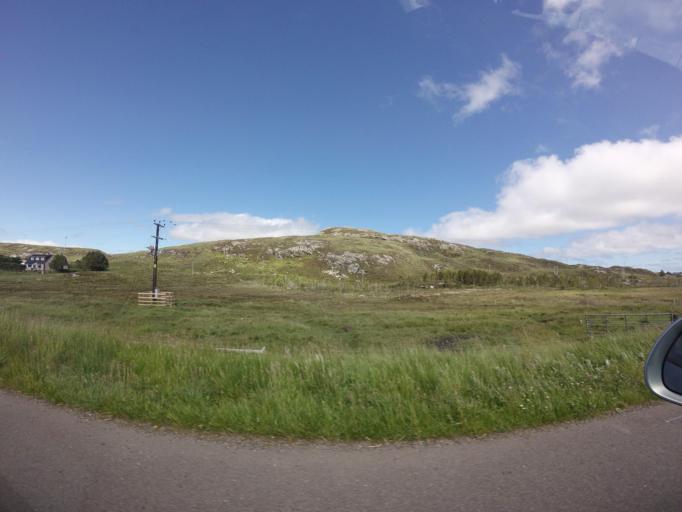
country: GB
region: Scotland
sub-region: Eilean Siar
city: Stornoway
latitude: 58.1062
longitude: -6.5292
